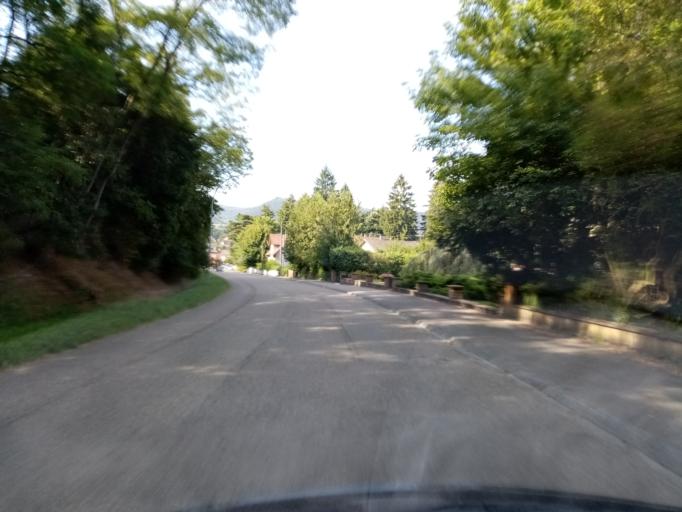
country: FR
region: Alsace
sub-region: Departement du Bas-Rhin
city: Ville
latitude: 48.3458
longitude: 7.3094
